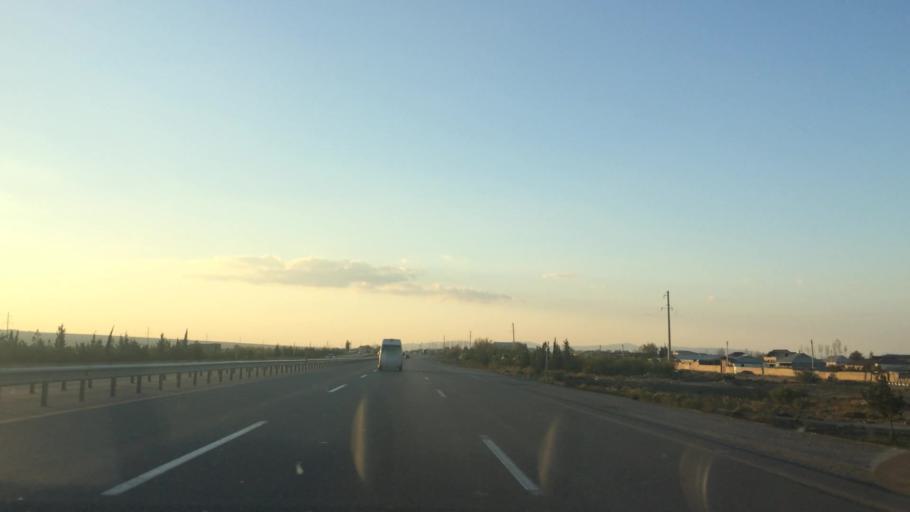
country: AZ
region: Haciqabul
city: Haciqabul
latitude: 40.0043
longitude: 49.1653
